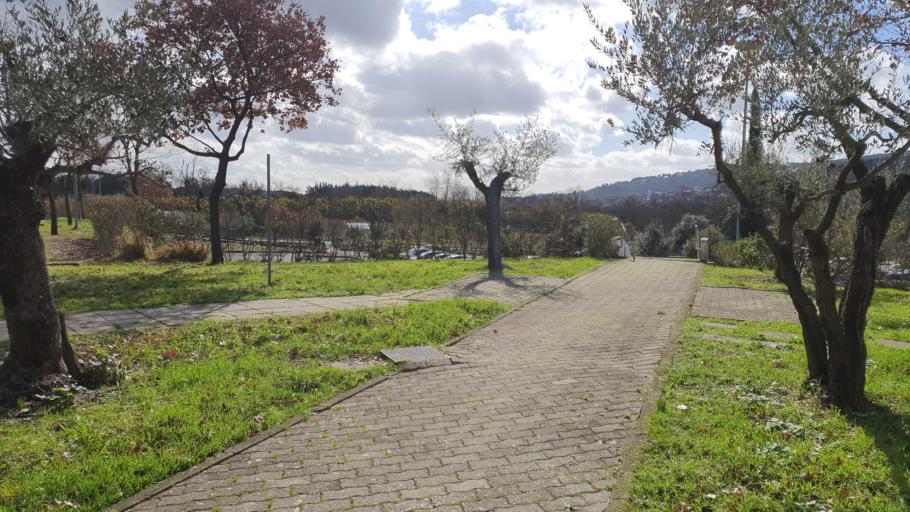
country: IT
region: Umbria
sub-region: Provincia di Perugia
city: Perugia
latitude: 43.1189
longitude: 12.3568
